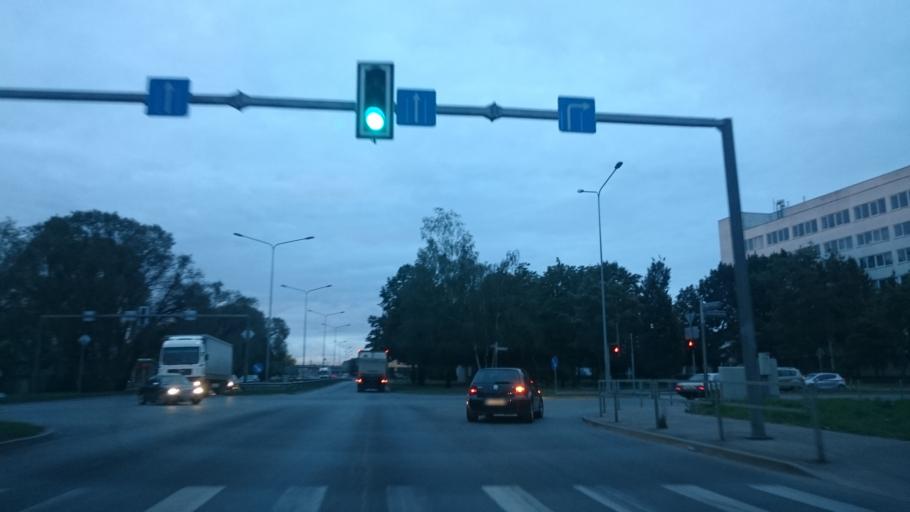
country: LV
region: Riga
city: Riga
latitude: 56.9258
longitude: 24.1879
